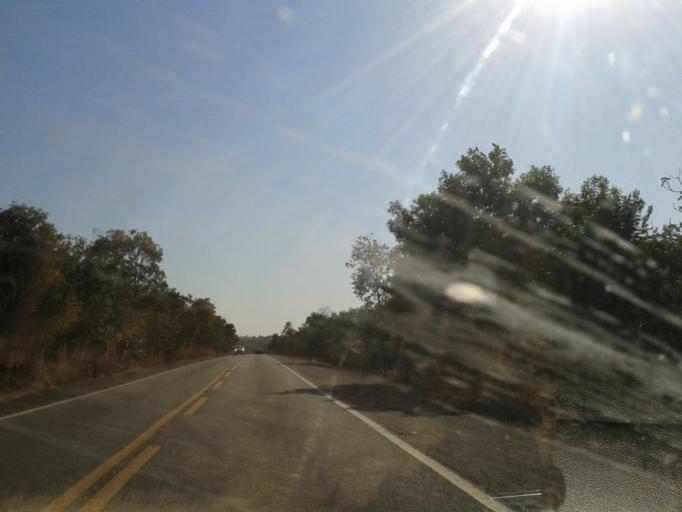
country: BR
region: Goias
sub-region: Mozarlandia
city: Mozarlandia
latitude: -14.8399
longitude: -50.5406
